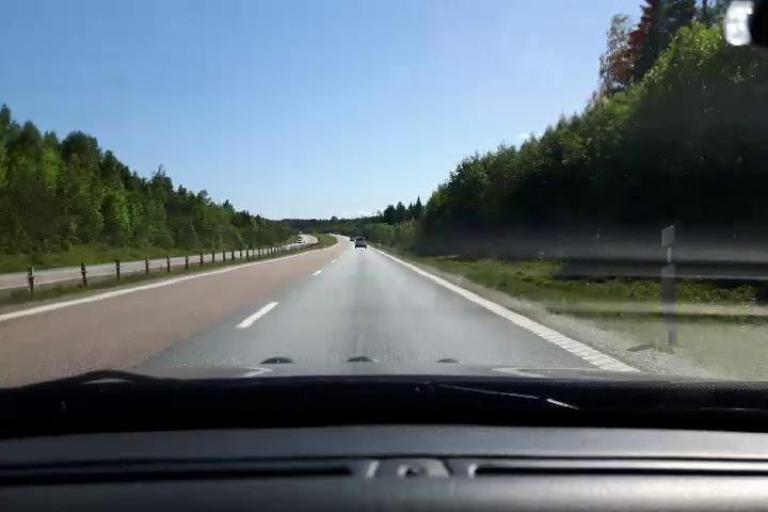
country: SE
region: Gaevleborg
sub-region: Hudiksvalls Kommun
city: Iggesund
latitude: 61.4971
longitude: 16.9848
